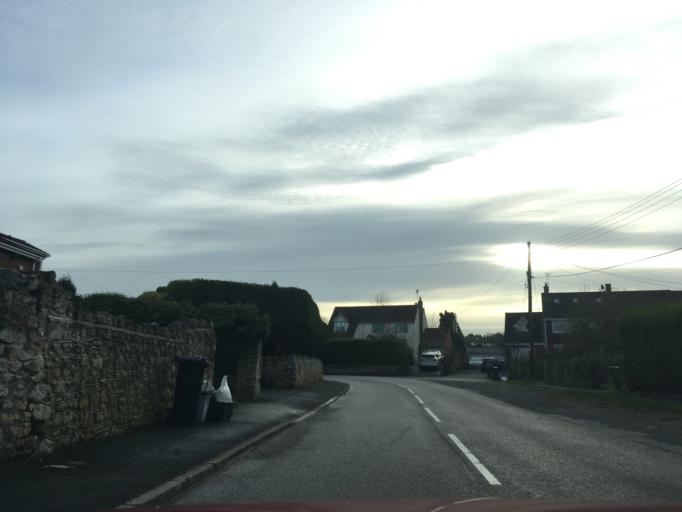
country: GB
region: England
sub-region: South Gloucestershire
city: Almondsbury
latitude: 51.5566
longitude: -2.5769
